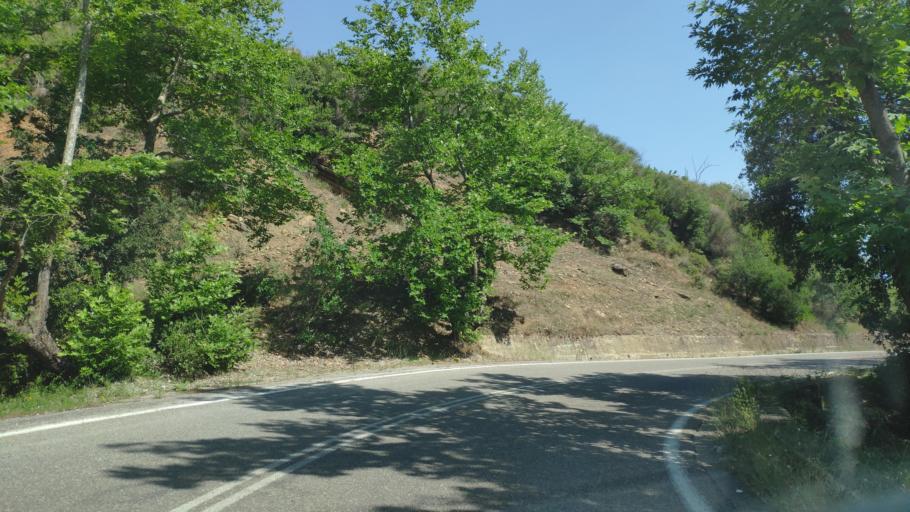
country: GR
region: West Greece
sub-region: Nomos Aitolias kai Akarnanias
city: Lepenou
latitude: 38.8016
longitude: 21.3328
